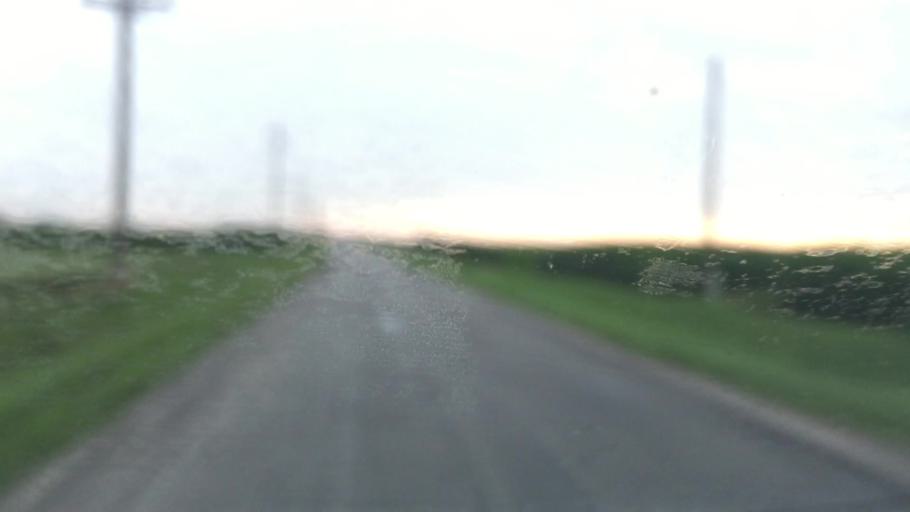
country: US
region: Iowa
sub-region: Lee County
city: Fort Madison
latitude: 40.5515
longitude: -91.2689
